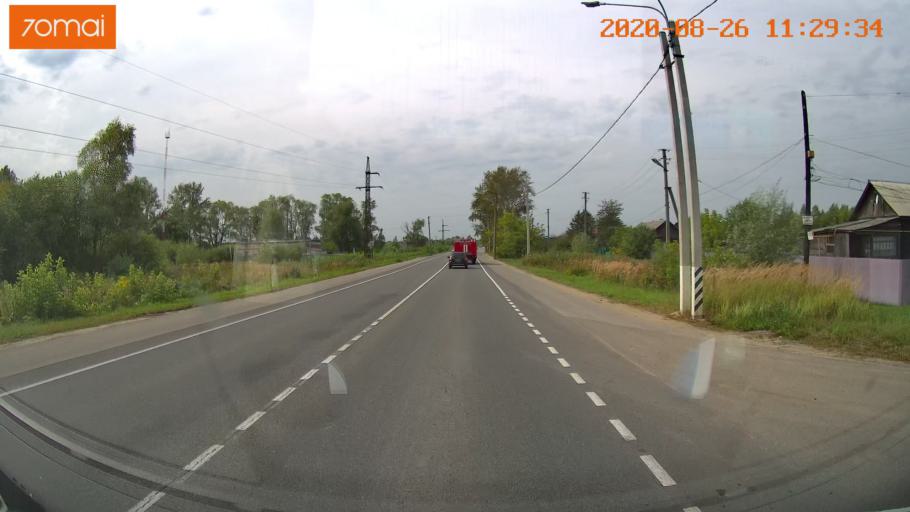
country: RU
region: Rjazan
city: Shilovo
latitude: 54.3190
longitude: 40.8974
